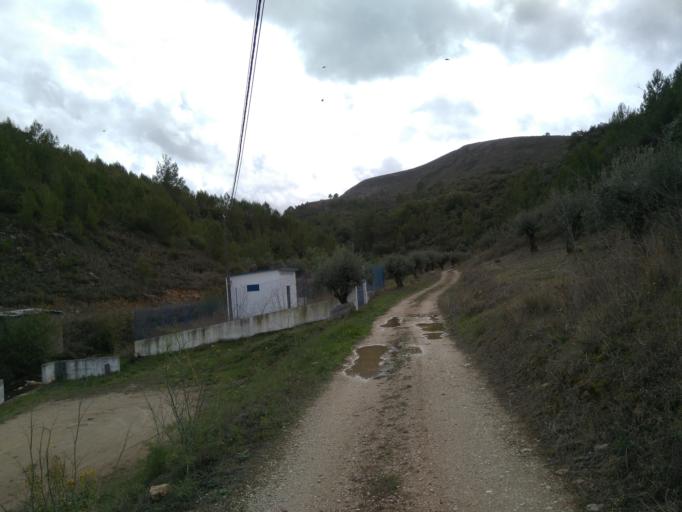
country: PT
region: Leiria
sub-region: Porto de Mos
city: Porto de Mos
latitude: 39.5827
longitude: -8.8192
